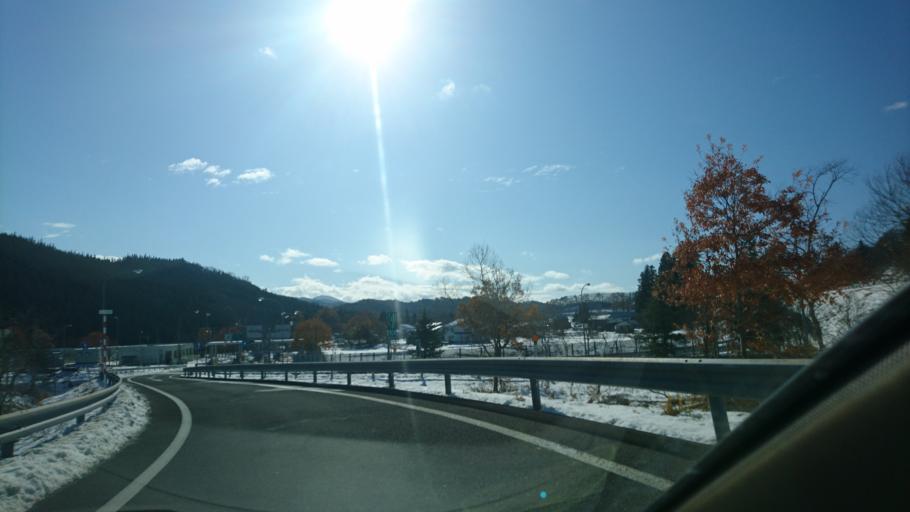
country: JP
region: Akita
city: Yokotemachi
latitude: 39.3134
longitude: 140.7478
